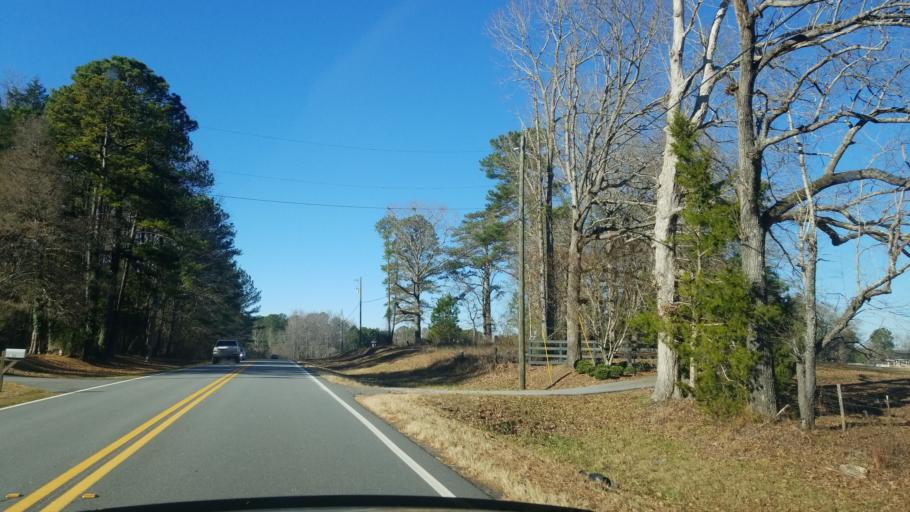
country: US
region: Georgia
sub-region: Harris County
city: Hamilton
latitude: 32.6718
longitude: -84.9053
